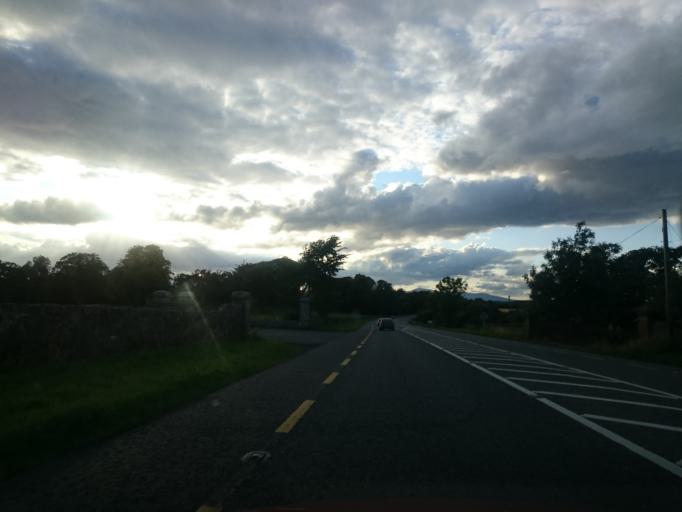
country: IE
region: Leinster
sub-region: Loch Garman
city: Enniscorthy
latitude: 52.4514
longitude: -6.5516
